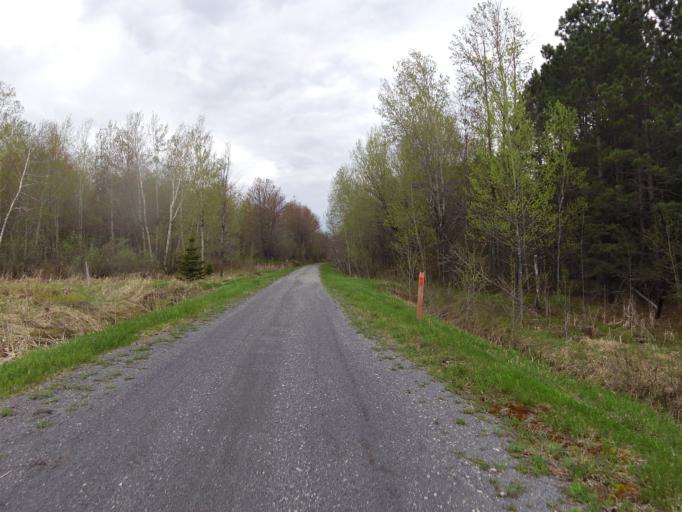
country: CA
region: Quebec
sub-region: Outaouais
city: Papineauville
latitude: 45.5159
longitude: -74.9330
